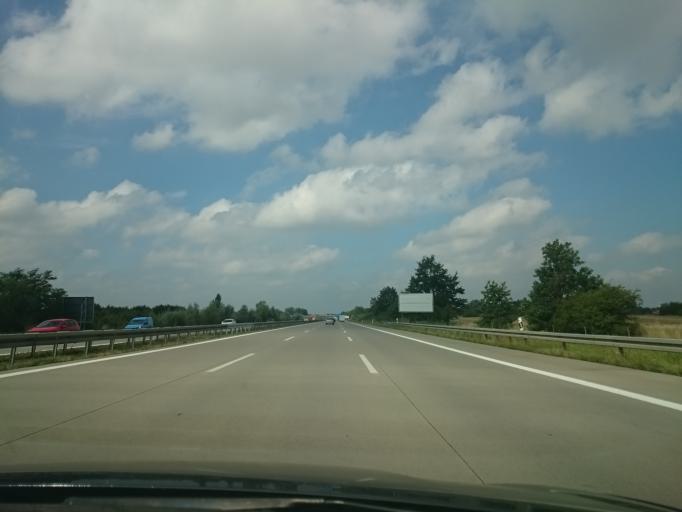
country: DE
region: Brandenburg
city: Ahrensfelde
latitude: 52.5877
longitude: 13.6261
